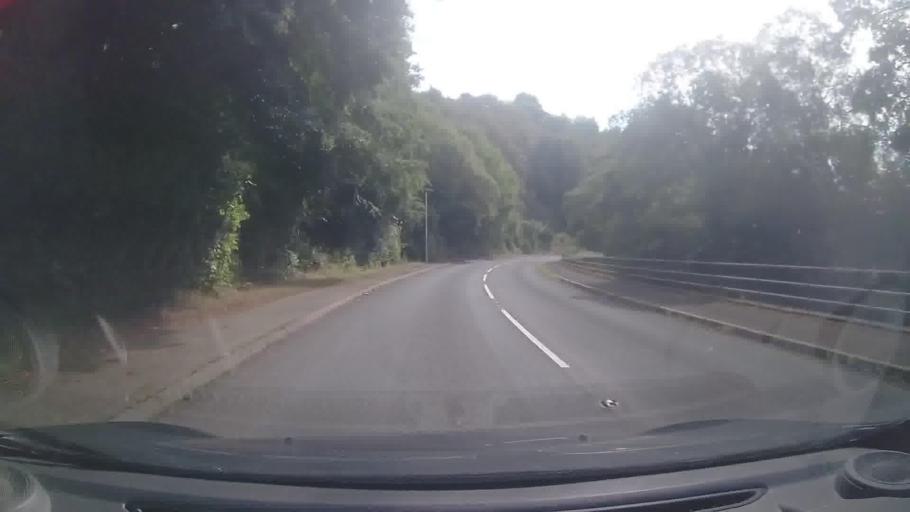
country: GB
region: Wales
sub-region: Sir Powys
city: Mochdre
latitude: 52.3926
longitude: -3.3255
